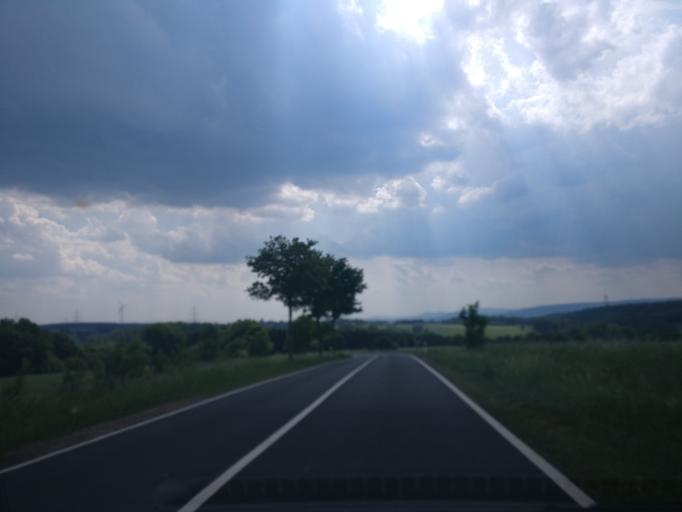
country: DE
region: Hesse
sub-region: Regierungsbezirk Kassel
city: Fuldatal
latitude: 51.3680
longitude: 9.6066
